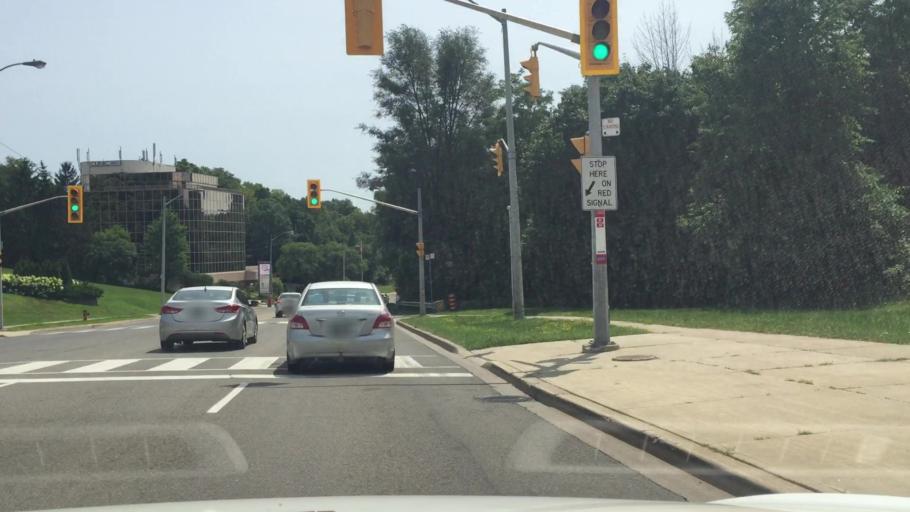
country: CA
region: Ontario
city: Willowdale
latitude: 43.7269
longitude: -79.3509
